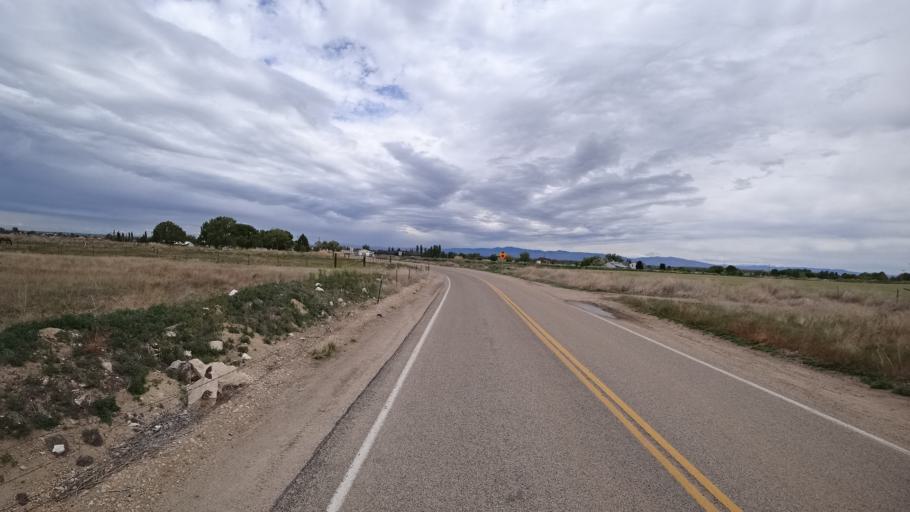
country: US
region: Idaho
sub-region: Ada County
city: Kuna
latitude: 43.4739
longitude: -116.4339
